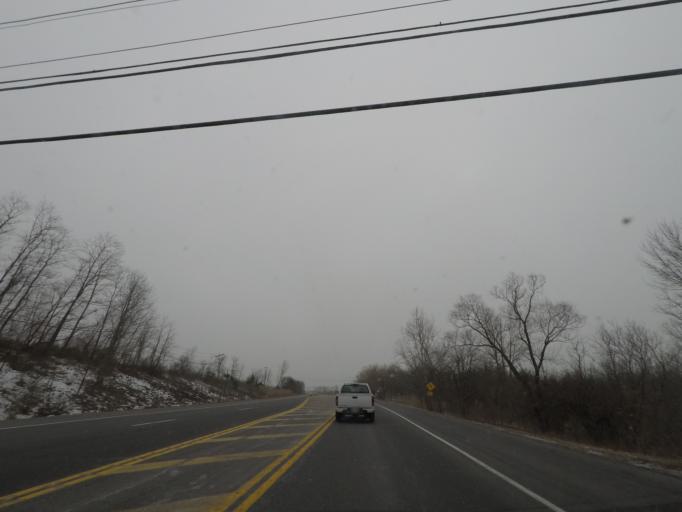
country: US
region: New York
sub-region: Albany County
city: Delmar
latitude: 42.5582
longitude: -73.8084
